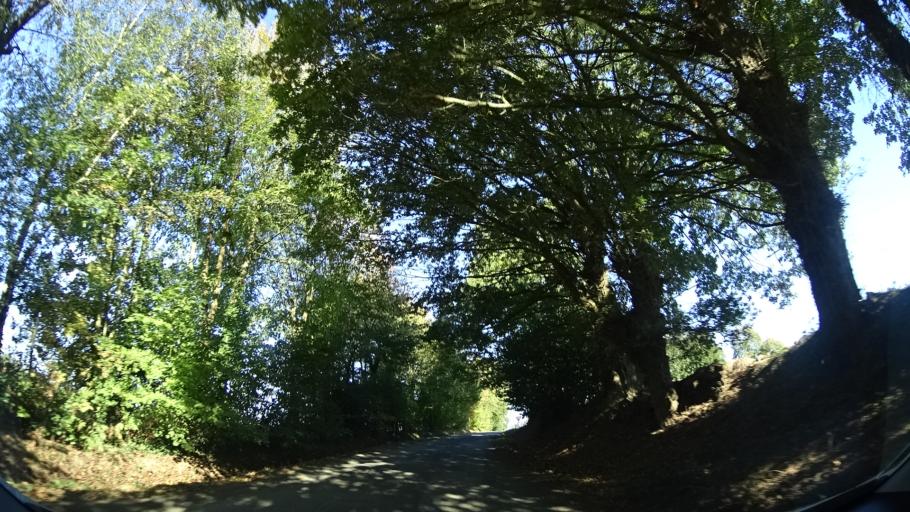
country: FR
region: Brittany
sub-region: Departement d'Ille-et-Vilaine
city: Geveze
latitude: 48.2126
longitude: -1.7753
